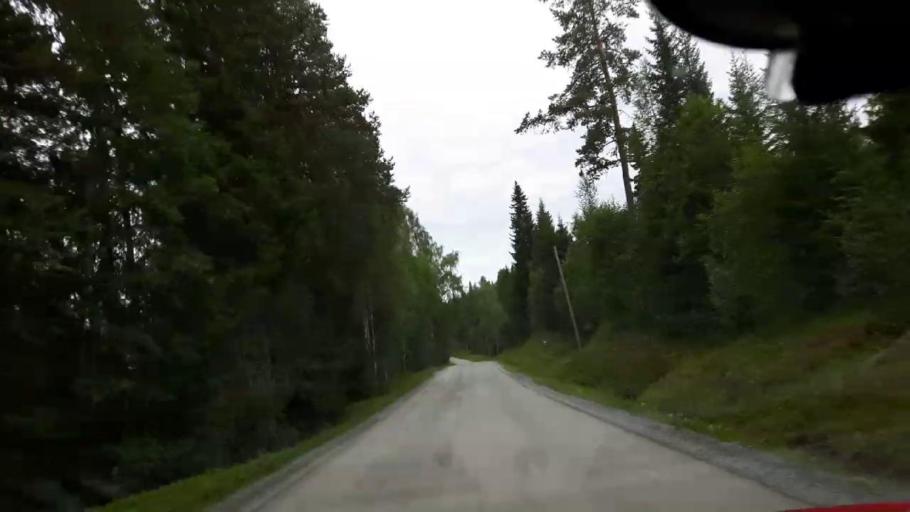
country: SE
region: Jaemtland
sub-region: Braecke Kommun
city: Braecke
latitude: 63.0879
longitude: 15.2615
